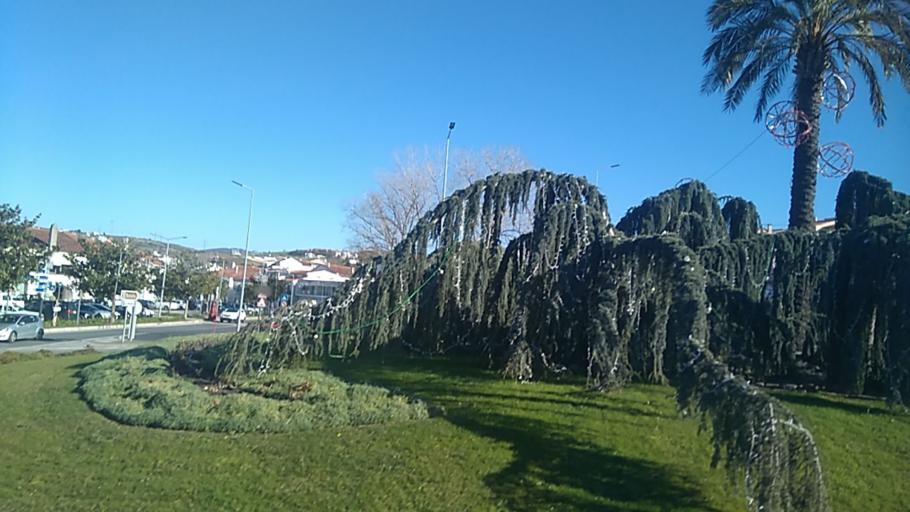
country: PT
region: Leiria
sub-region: Batalha
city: Batalha
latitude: 39.6569
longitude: -8.8269
